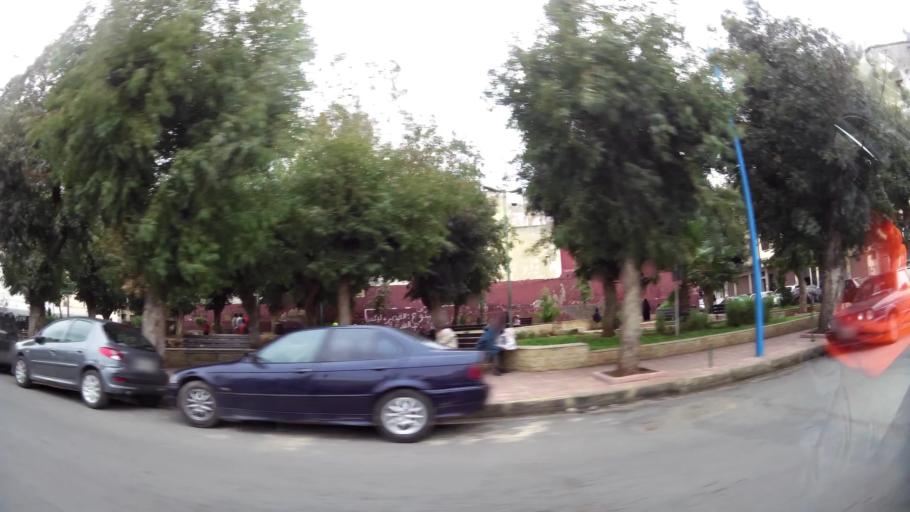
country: MA
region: Grand Casablanca
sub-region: Casablanca
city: Casablanca
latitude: 33.5673
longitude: -7.6091
